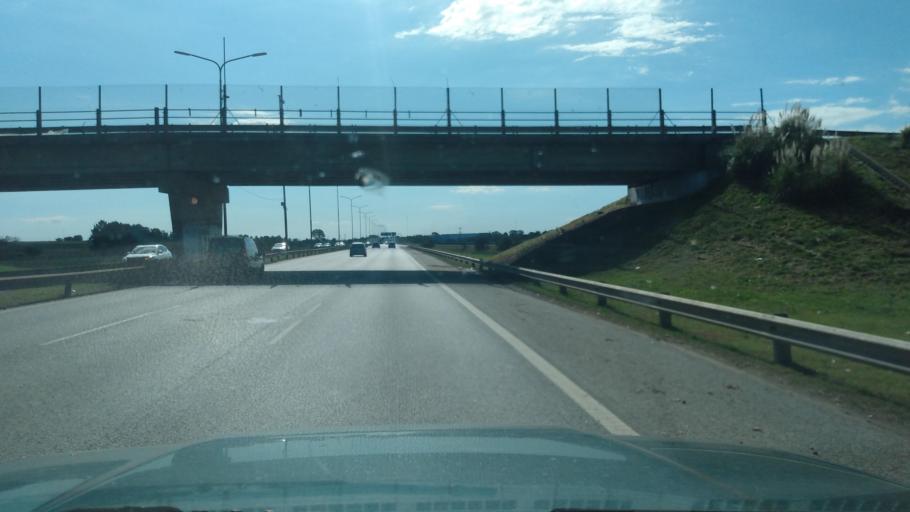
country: AR
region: Buenos Aires
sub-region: Partido de General San Martin
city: General San Martin
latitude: -34.5176
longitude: -58.5908
